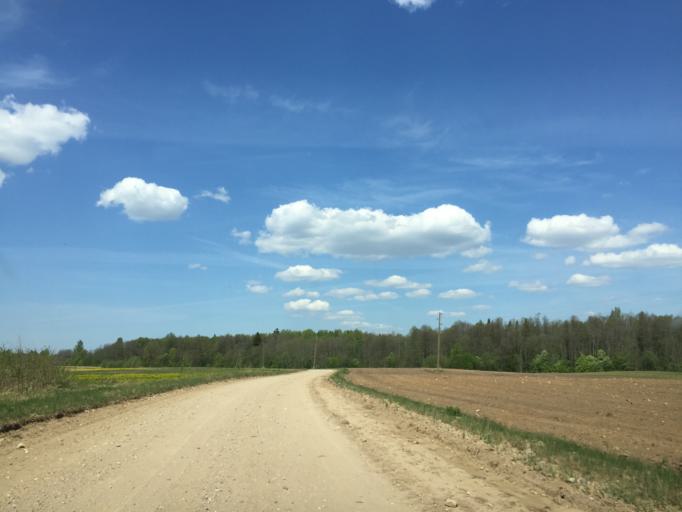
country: LV
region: Limbazu Rajons
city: Limbazi
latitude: 57.3771
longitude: 24.6273
